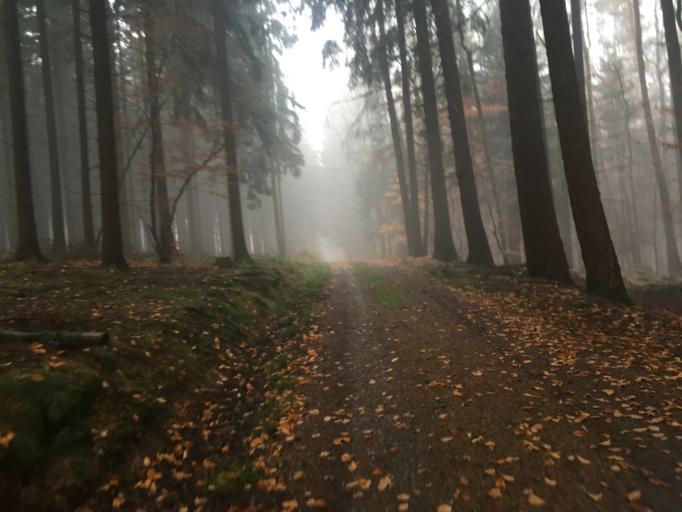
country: DE
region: Baden-Wuerttemberg
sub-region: Karlsruhe Region
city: Heddesbach
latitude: 49.4521
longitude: 8.8457
